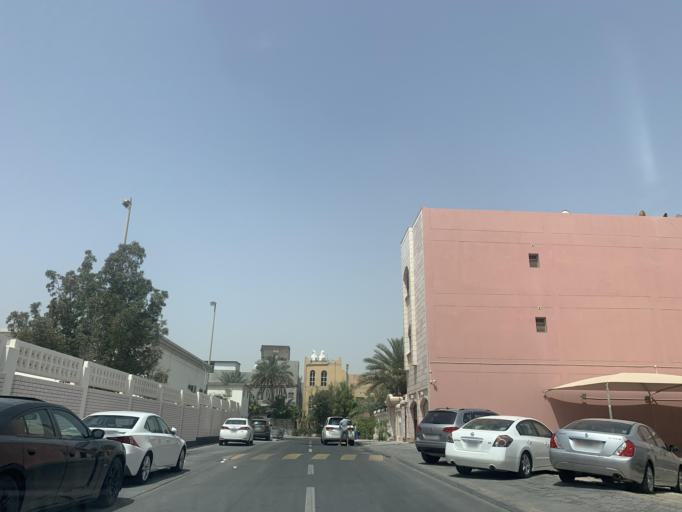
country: BH
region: Northern
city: Madinat `Isa
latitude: 26.1504
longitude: 50.5267
